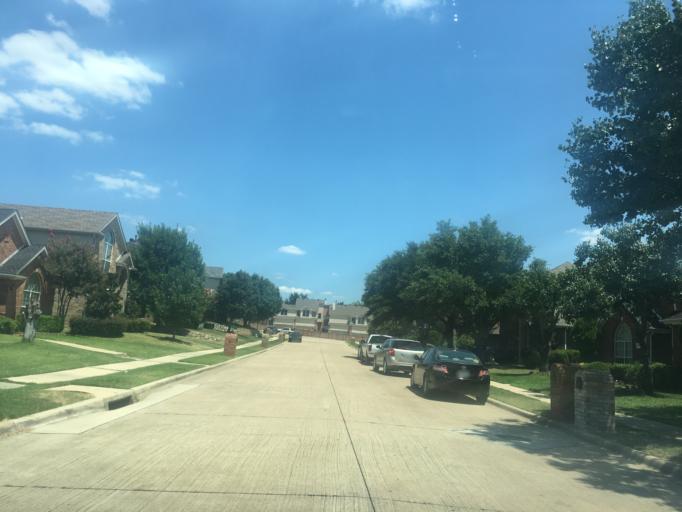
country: US
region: Texas
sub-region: Denton County
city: Lewisville
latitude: 33.0207
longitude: -96.9999
